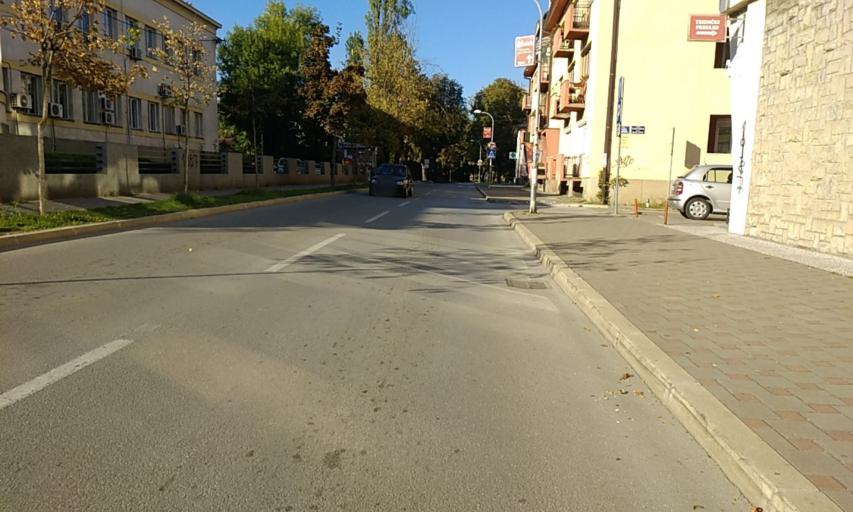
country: BA
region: Republika Srpska
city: Banja Luka
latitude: 44.7716
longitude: 17.1856
